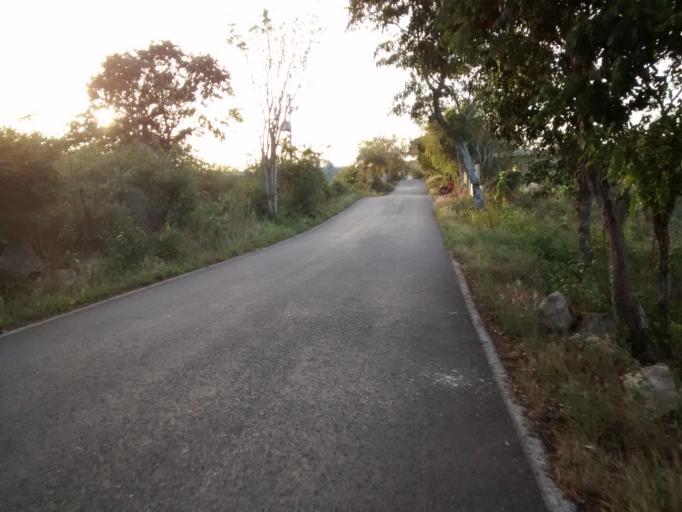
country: MX
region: Yucatan
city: Valladolid
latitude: 20.6818
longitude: -88.1664
